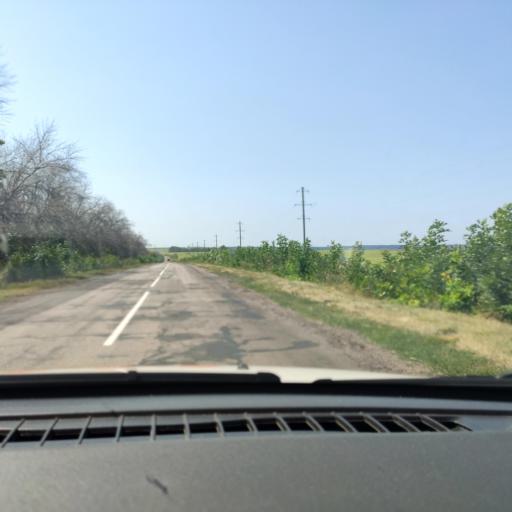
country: RU
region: Voronezj
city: Ol'khovatka
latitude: 50.6026
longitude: 39.3100
